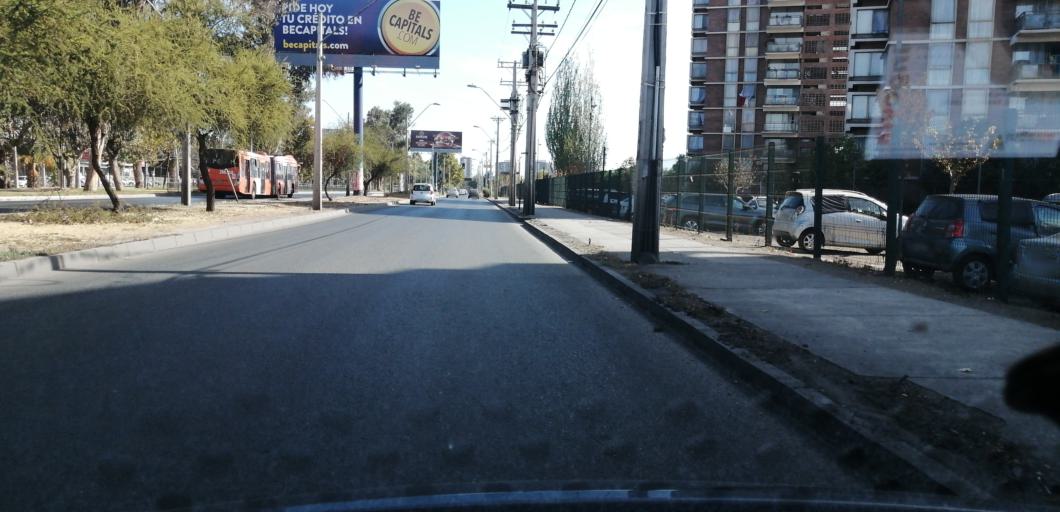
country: CL
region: Santiago Metropolitan
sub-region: Provincia de Santiago
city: Lo Prado
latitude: -33.4645
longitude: -70.7254
